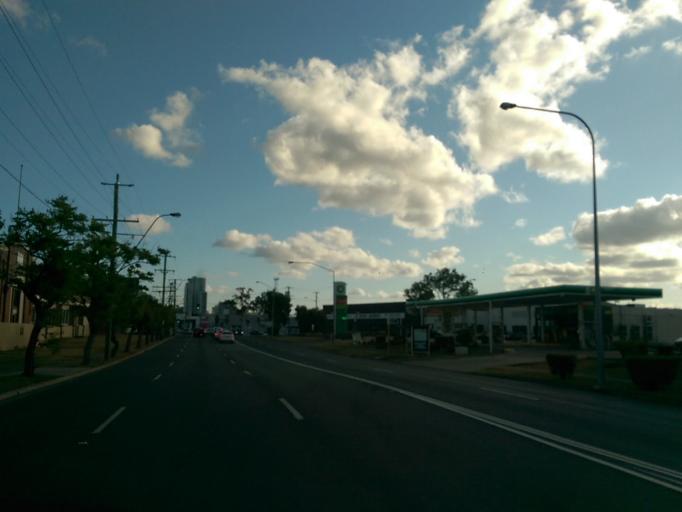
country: AU
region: Queensland
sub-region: Brisbane
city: Wooloowin
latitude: -27.4352
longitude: 153.0420
